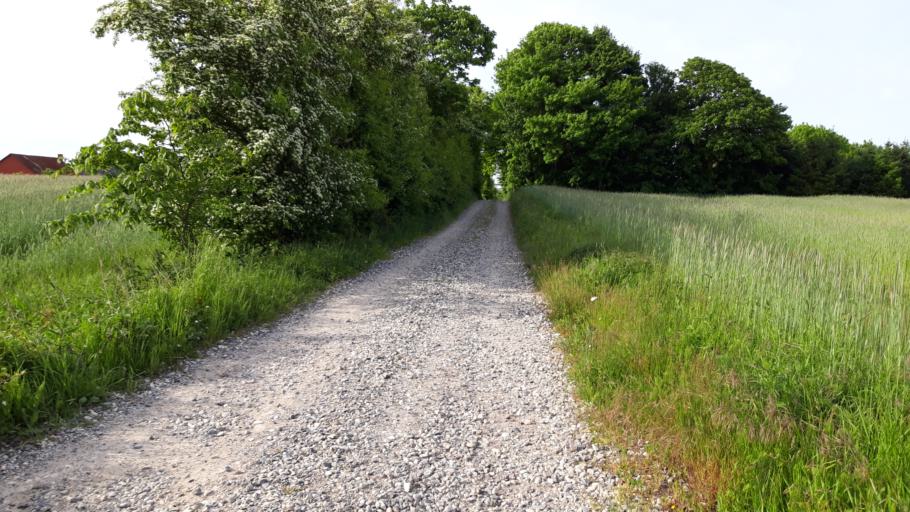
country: DK
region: Central Jutland
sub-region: Arhus Kommune
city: Lystrup
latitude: 56.2302
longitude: 10.1967
